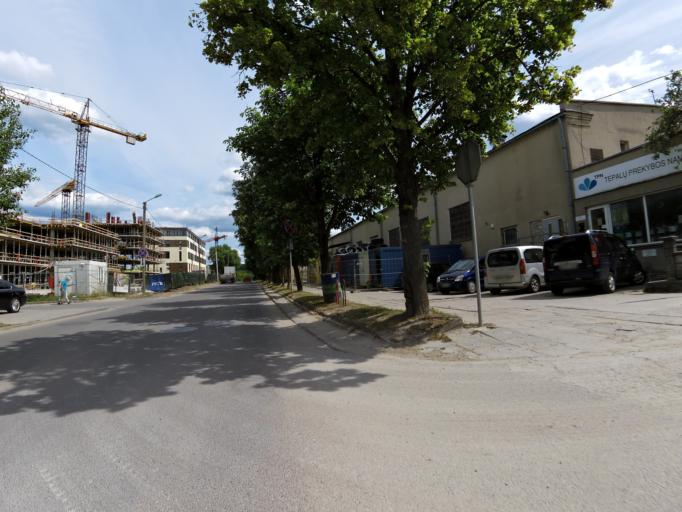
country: LT
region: Vilnius County
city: Rasos
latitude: 54.6776
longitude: 25.3163
